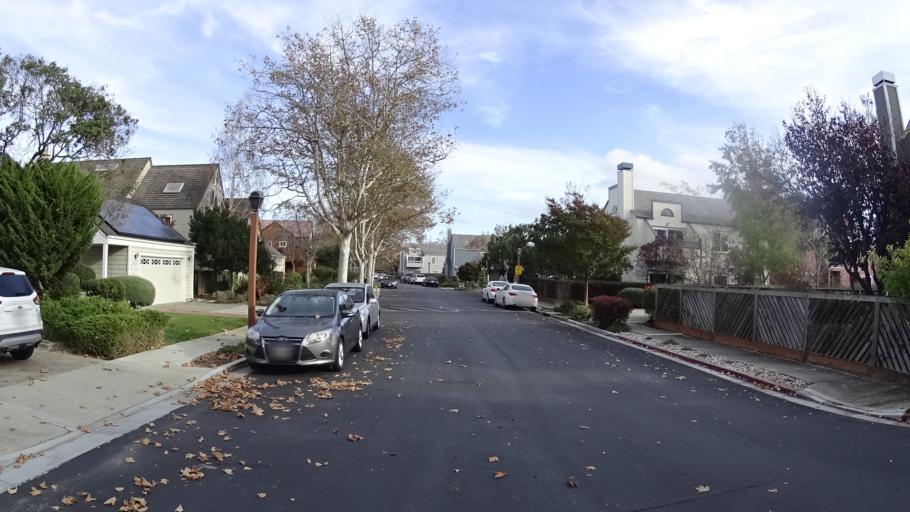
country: US
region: California
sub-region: San Mateo County
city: Foster City
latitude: 37.5435
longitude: -122.2675
